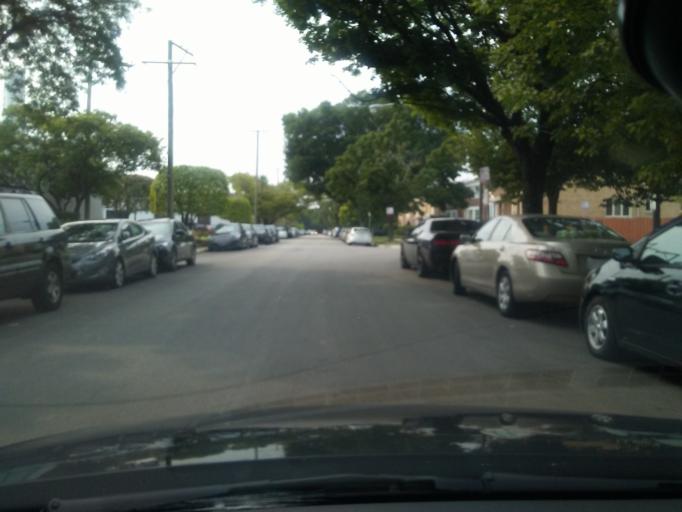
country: US
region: Illinois
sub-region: Cook County
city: Lincolnwood
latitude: 41.9905
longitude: -87.7337
